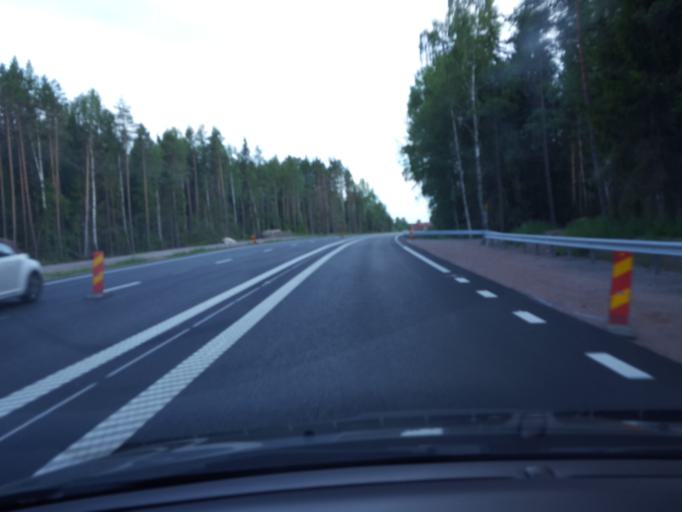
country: SE
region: Uppsala
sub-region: Osthammars Kommun
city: Gimo
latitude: 60.0995
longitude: 18.1255
